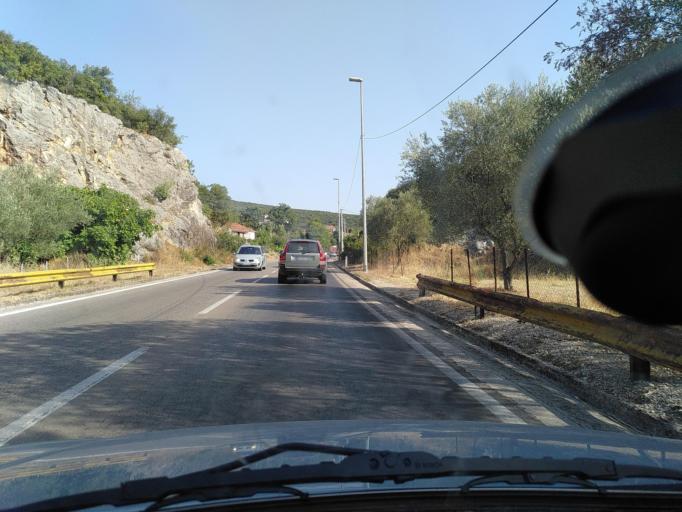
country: ME
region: Ulcinj
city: Ulcinj
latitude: 41.9540
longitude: 19.1917
